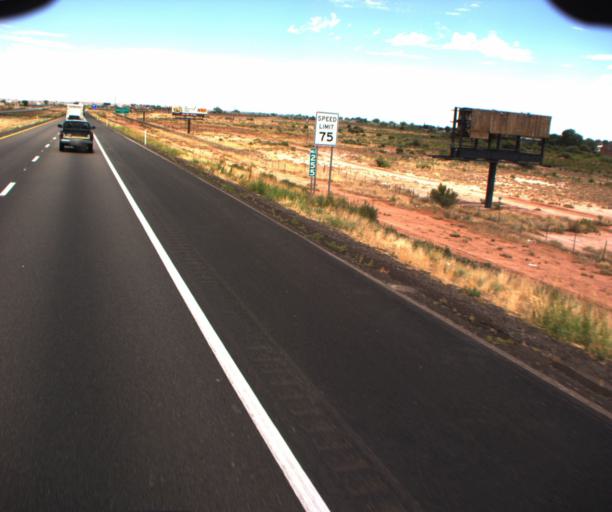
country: US
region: Arizona
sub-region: Navajo County
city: Winslow
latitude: 35.0258
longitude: -110.6822
